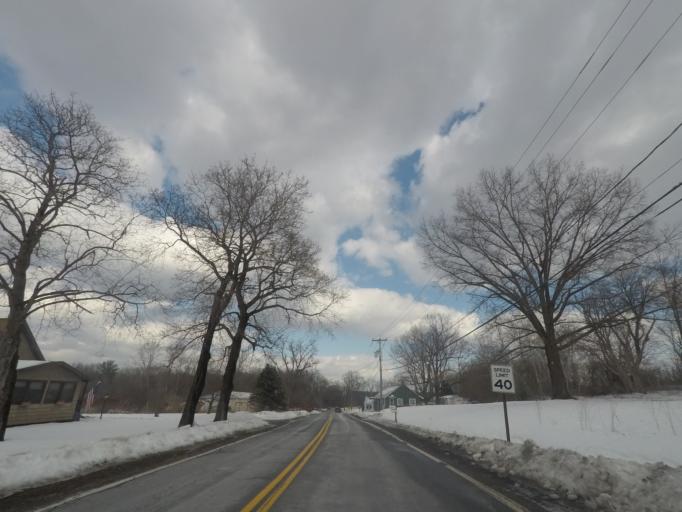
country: US
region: New York
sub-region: Saratoga County
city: Country Knolls
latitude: 42.9085
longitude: -73.7742
